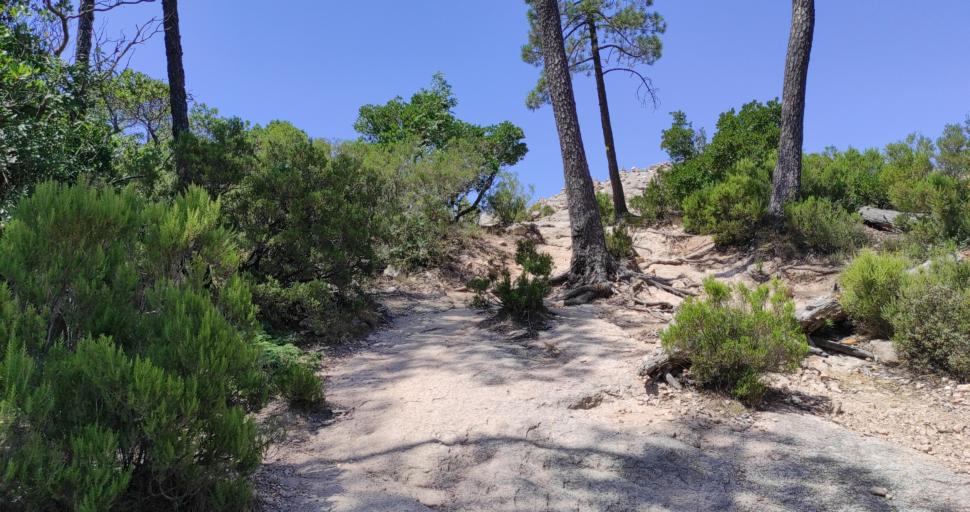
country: FR
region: Corsica
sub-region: Departement de la Corse-du-Sud
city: Zonza
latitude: 41.6841
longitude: 9.2051
